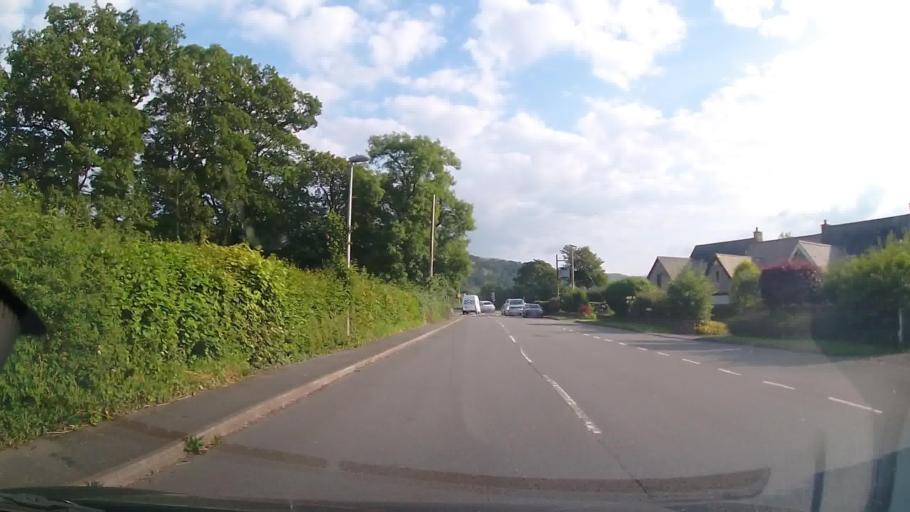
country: GB
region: Wales
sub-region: Gwynedd
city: Bala
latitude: 52.9064
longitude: -3.5946
